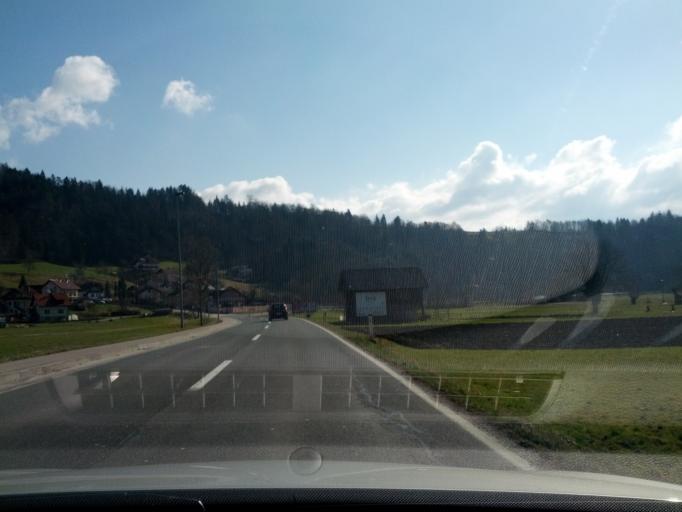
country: SI
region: Litija
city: Litija
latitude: 46.0917
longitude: 14.8297
